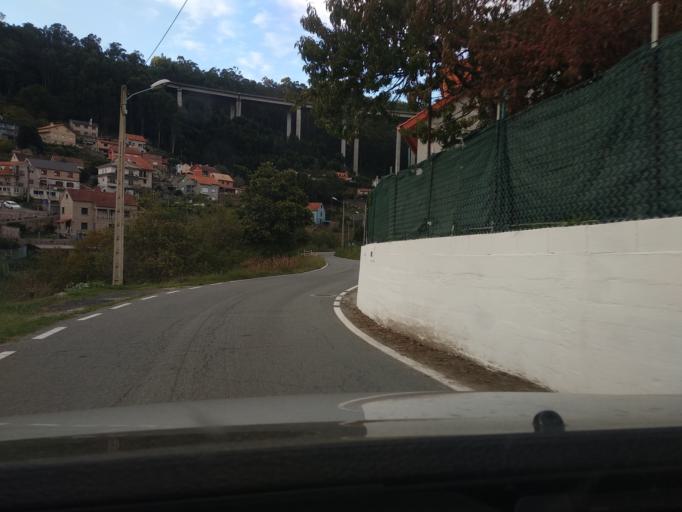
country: ES
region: Galicia
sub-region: Provincia de Pontevedra
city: Moana
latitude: 42.2948
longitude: -8.6799
